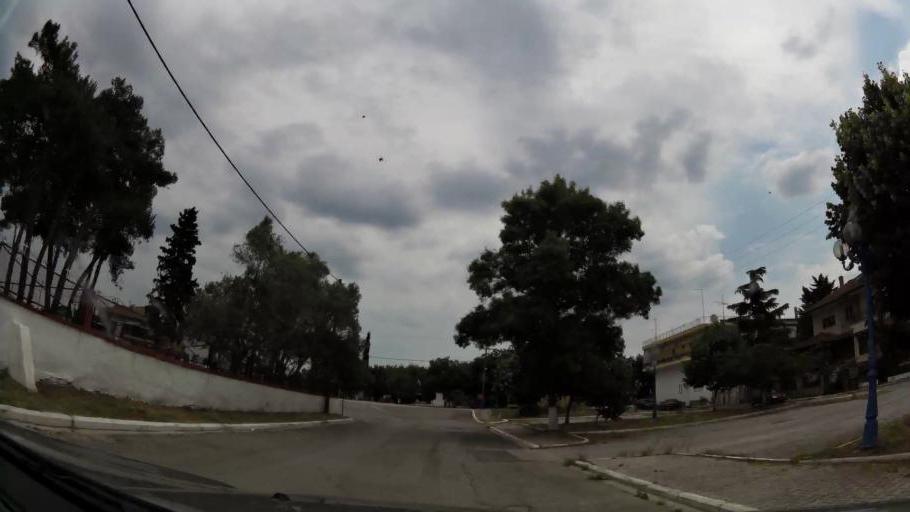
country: GR
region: Central Macedonia
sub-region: Nomos Pierias
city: Kallithea
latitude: 40.2769
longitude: 22.5783
